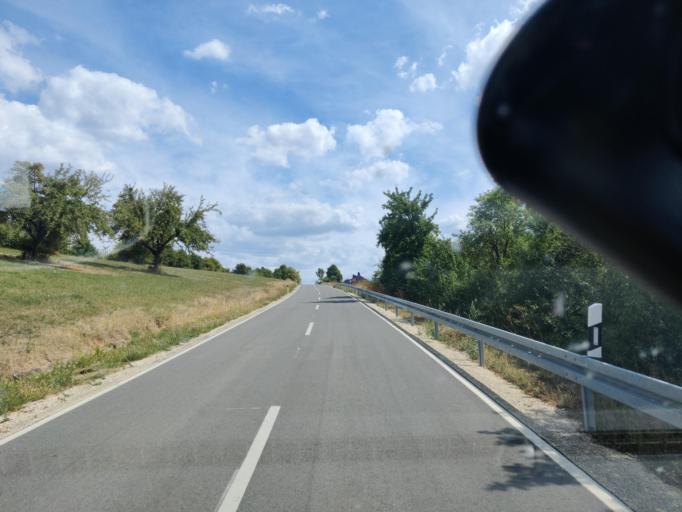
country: DE
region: Bavaria
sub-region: Regierungsbezirk Mittelfranken
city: Heideck
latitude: 49.1234
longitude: 11.1273
